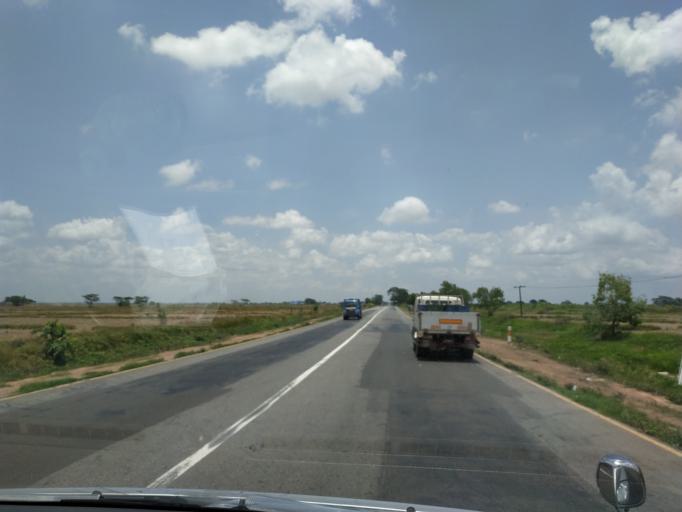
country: MM
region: Bago
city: Bago
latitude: 17.4630
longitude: 96.5925
